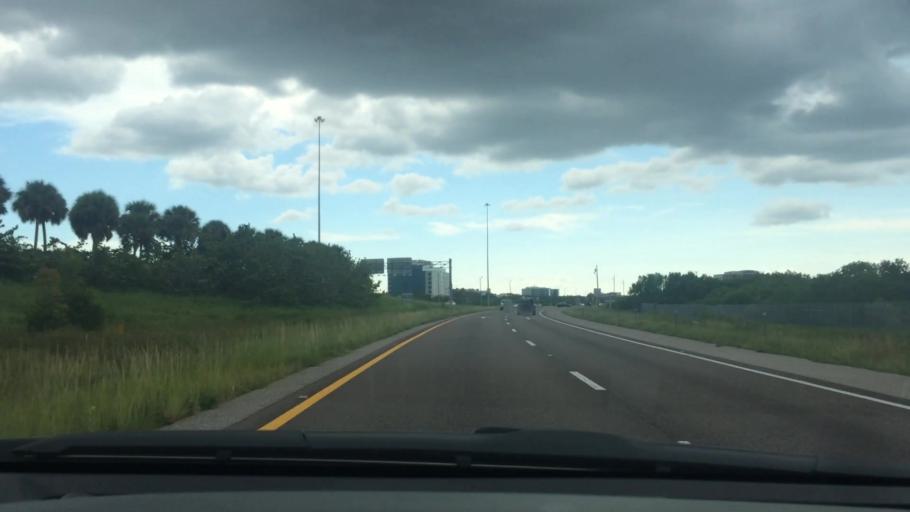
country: US
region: Florida
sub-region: Pinellas County
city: Feather Sound
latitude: 27.8943
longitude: -82.6479
